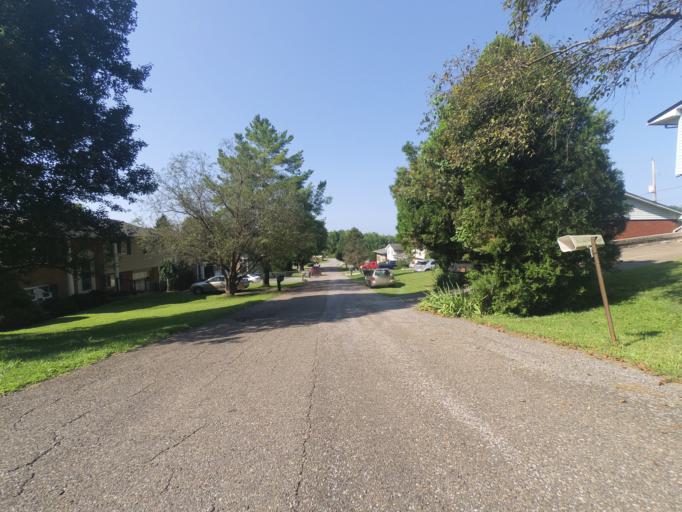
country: US
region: West Virginia
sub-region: Cabell County
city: Huntington
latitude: 38.4328
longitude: -82.4524
